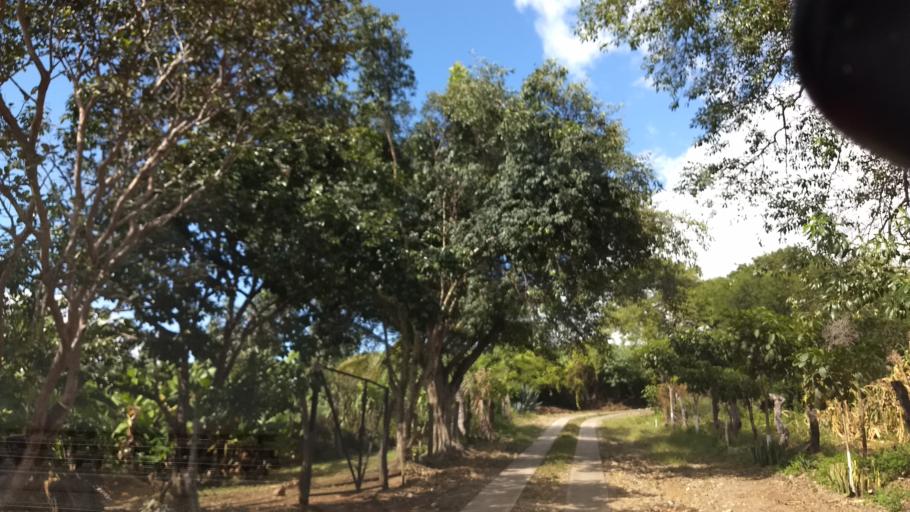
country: MX
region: Colima
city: Suchitlan
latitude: 19.4546
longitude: -103.7729
